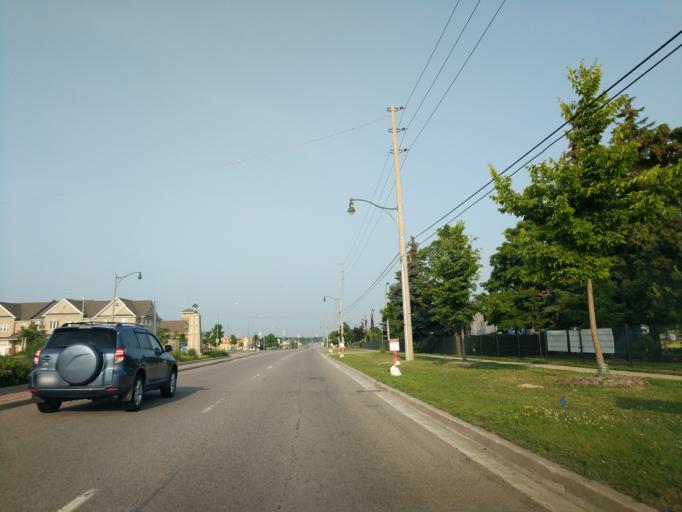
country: CA
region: Ontario
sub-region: York
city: Richmond Hill
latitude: 43.8979
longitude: -79.3987
